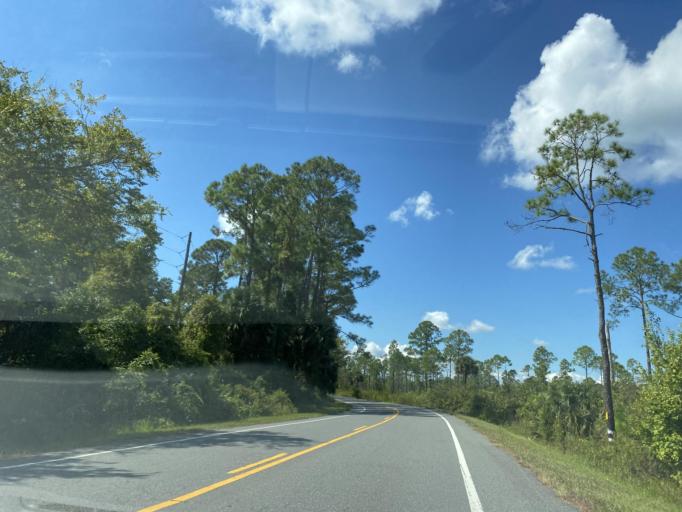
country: US
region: Florida
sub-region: Lake County
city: Lake Mack-Forest Hills
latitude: 29.0166
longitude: -81.4722
